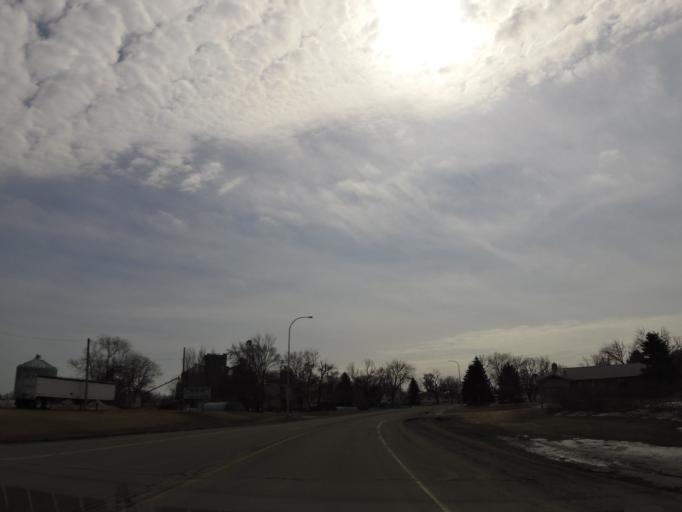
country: US
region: North Dakota
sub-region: Walsh County
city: Grafton
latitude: 48.2953
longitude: -97.3721
